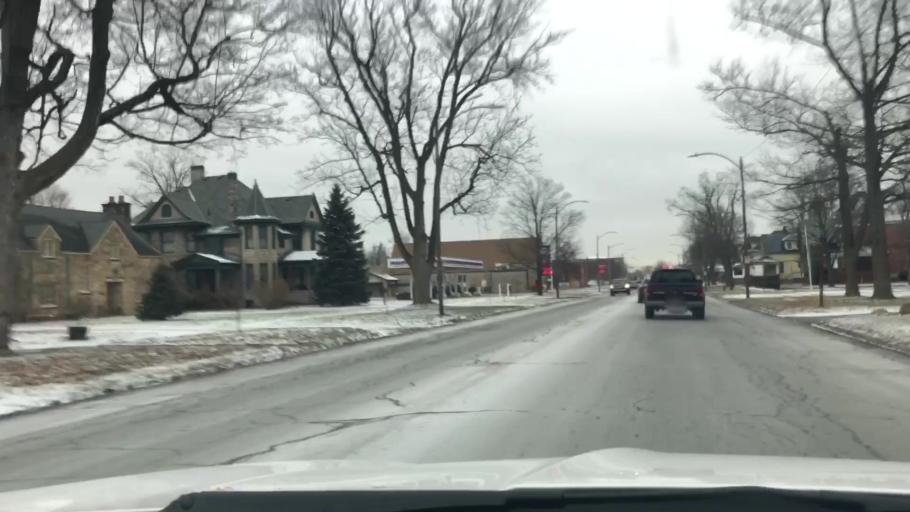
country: US
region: Indiana
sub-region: Fulton County
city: Rochester
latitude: 41.0620
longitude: -86.2163
